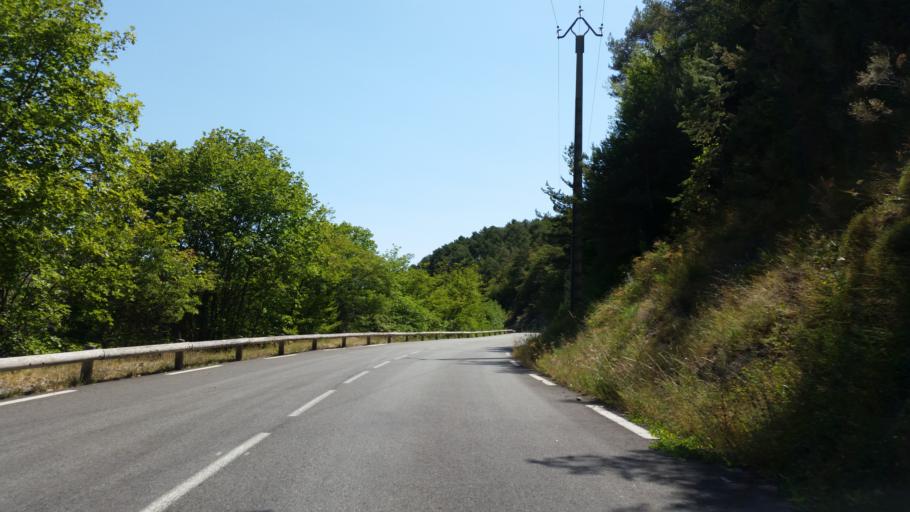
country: FR
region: Provence-Alpes-Cote d'Azur
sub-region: Departement des Alpes-Maritimes
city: Breil-sur-Roya
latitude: 43.9149
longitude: 7.4779
